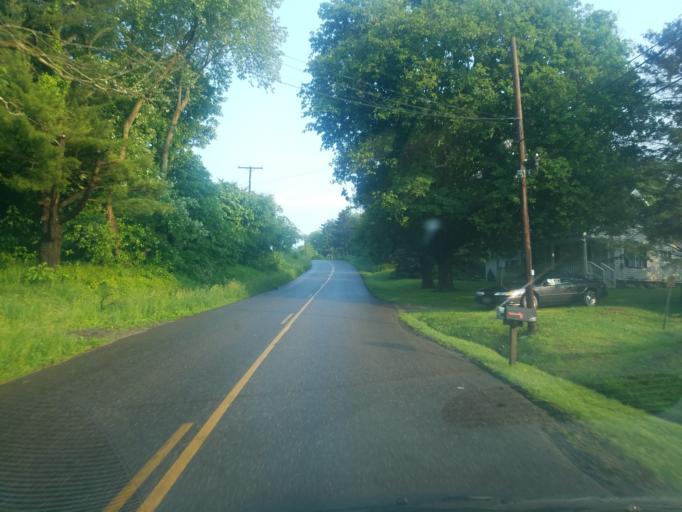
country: US
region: Ohio
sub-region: Stark County
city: Minerva
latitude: 40.7159
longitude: -81.0922
